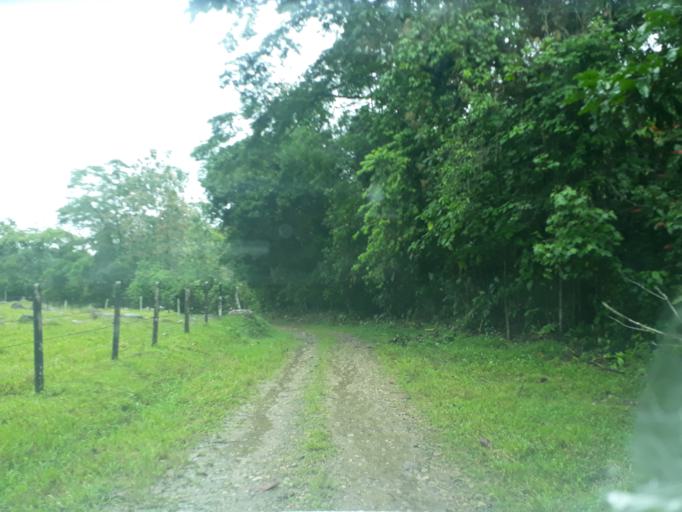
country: CO
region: Cundinamarca
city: Medina
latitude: 4.5292
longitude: -73.3661
